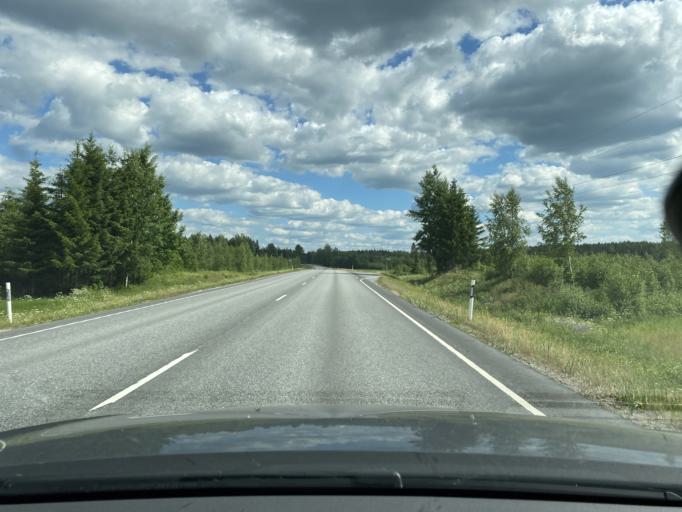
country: FI
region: Satakunta
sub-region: Pori
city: Huittinen
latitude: 61.1515
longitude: 22.7365
